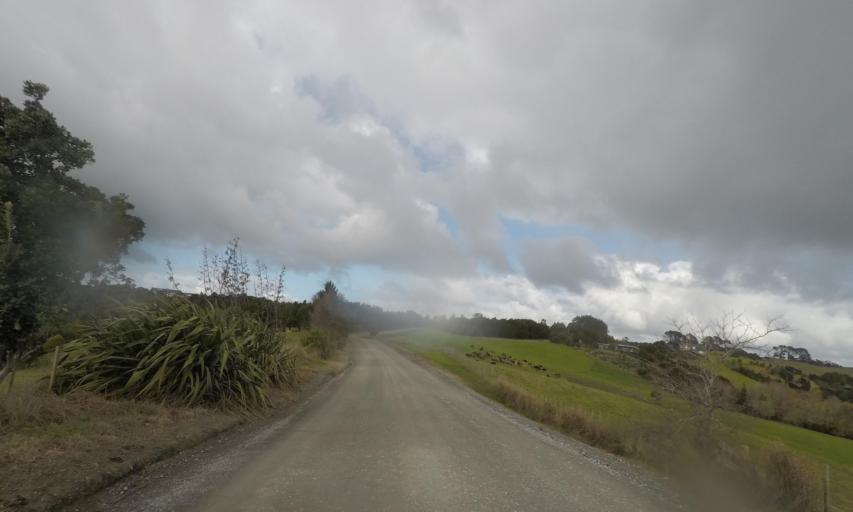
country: NZ
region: Auckland
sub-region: Auckland
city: Wellsford
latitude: -36.1662
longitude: 174.6024
